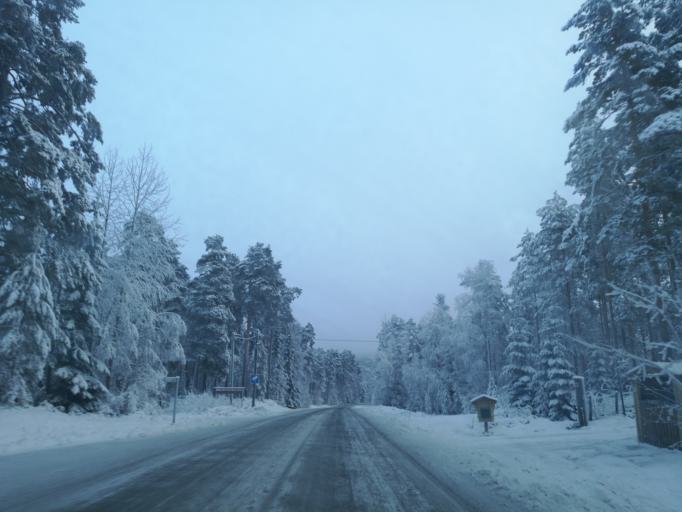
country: NO
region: Hedmark
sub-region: Grue
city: Kirkenaer
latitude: 60.3687
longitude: 12.3523
